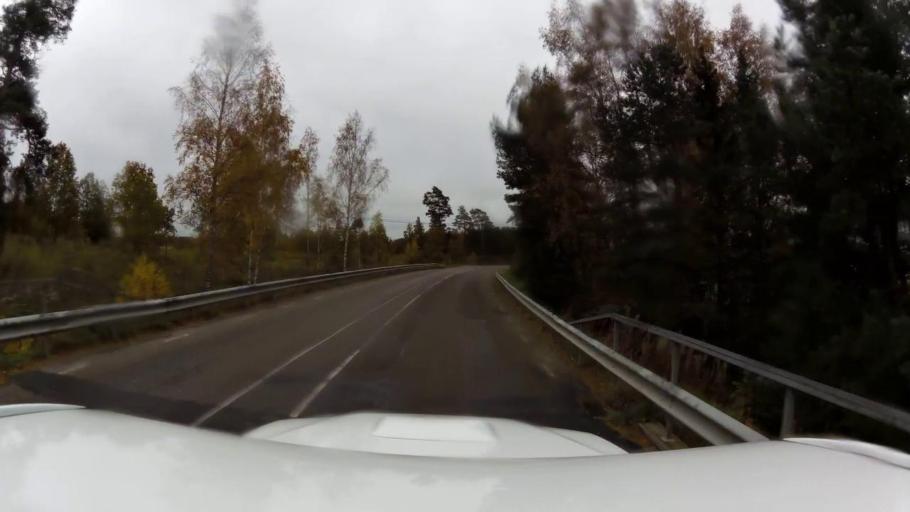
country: SE
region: OEstergoetland
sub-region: Linkopings Kommun
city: Linghem
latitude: 58.4413
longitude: 15.7142
